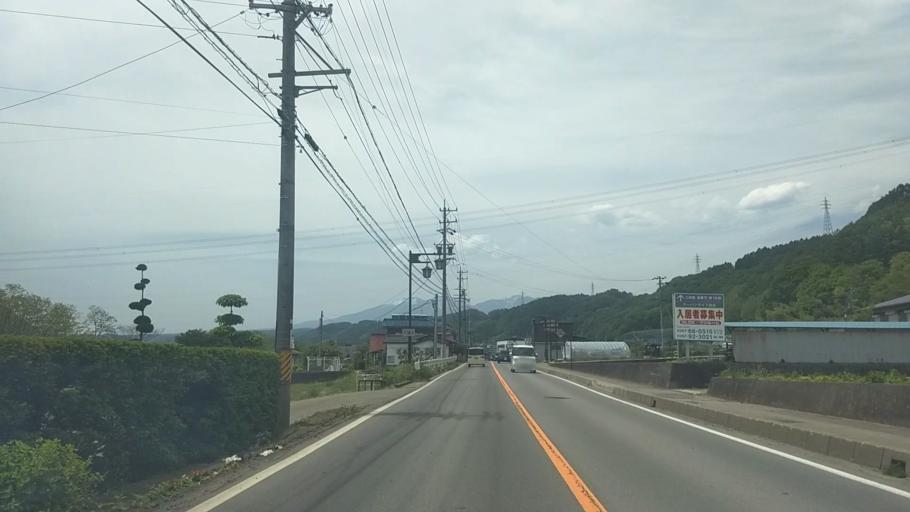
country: JP
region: Nagano
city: Saku
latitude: 36.1552
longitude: 138.4778
